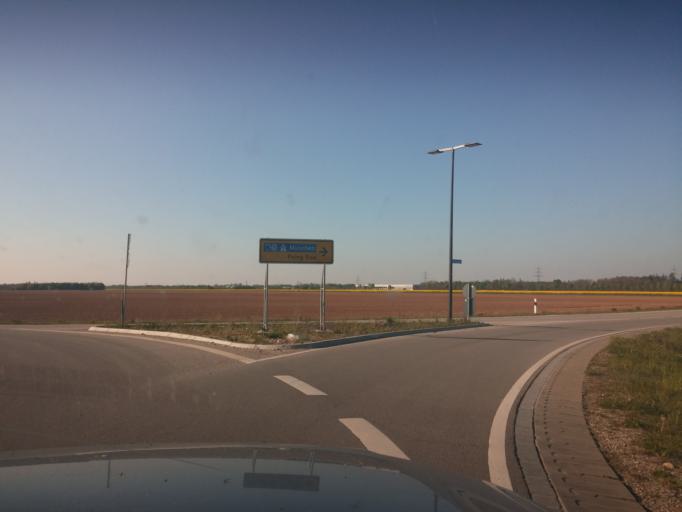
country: DE
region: Bavaria
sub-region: Upper Bavaria
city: Kirchheim bei Muenchen
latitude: 48.1483
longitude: 11.7804
